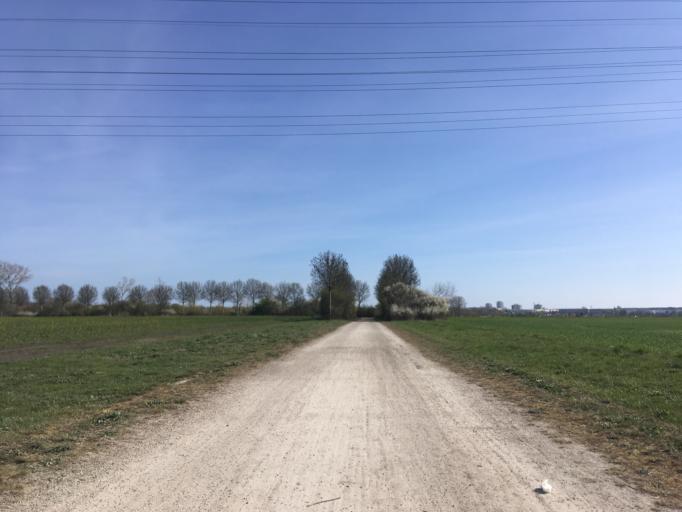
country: DE
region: Berlin
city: Wartenberg
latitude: 52.5934
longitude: 13.5071
